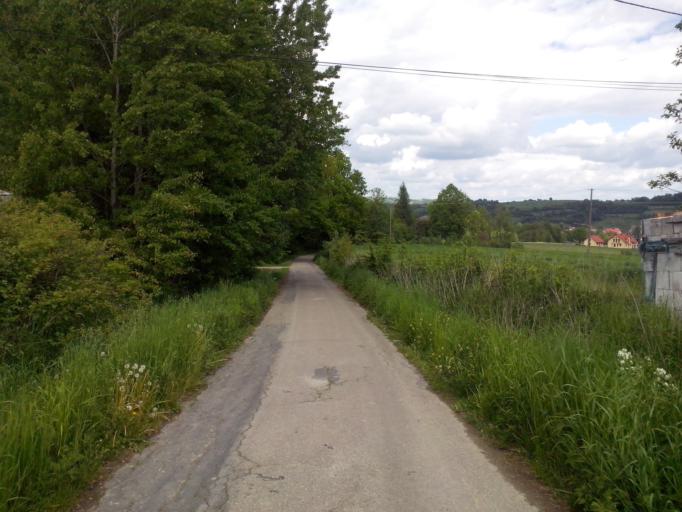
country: PL
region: Subcarpathian Voivodeship
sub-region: Powiat strzyzowski
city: Strzyzow
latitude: 49.8364
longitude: 21.8081
